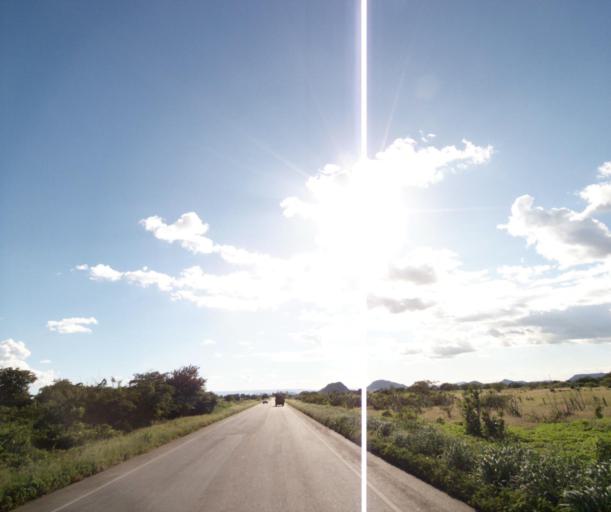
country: BR
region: Bahia
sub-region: Guanambi
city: Guanambi
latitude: -14.1599
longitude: -42.7125
